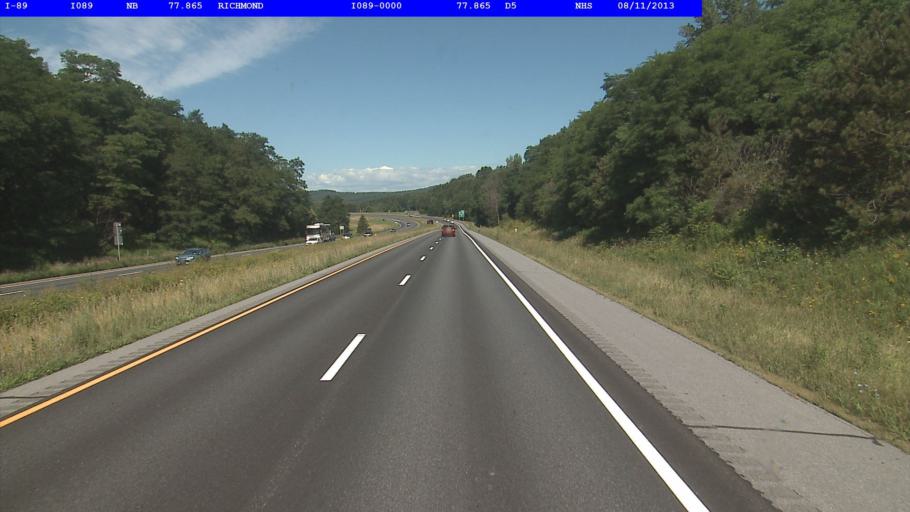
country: US
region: Vermont
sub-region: Chittenden County
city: Williston
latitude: 44.4205
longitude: -73.0011
